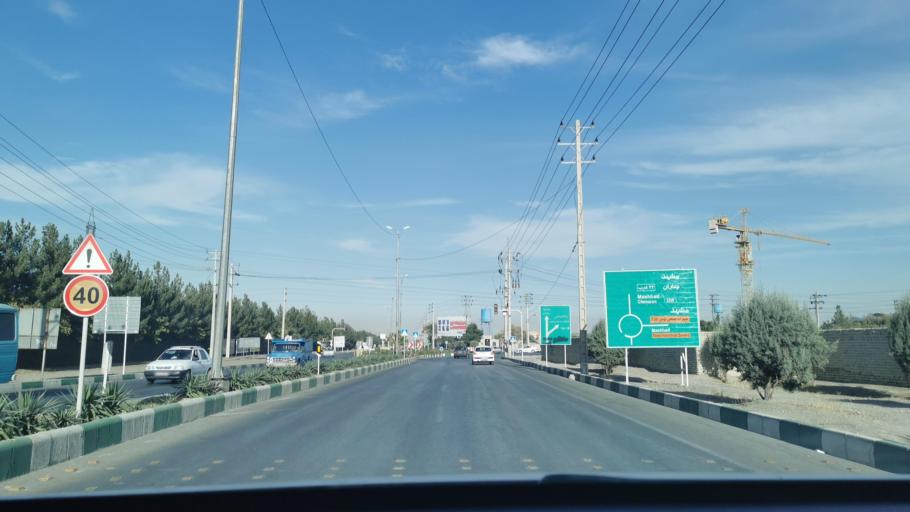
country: IR
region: Razavi Khorasan
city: Torqabeh
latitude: 36.4290
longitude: 59.4175
